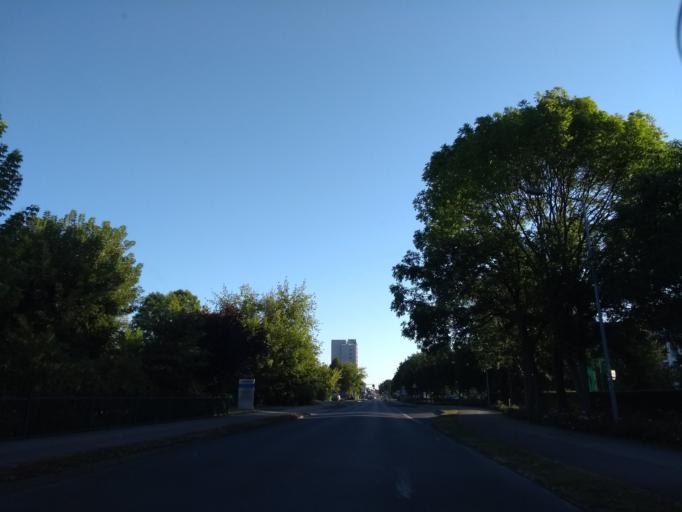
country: DE
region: Brandenburg
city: Lubbenau
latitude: 51.8561
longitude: 13.9507
